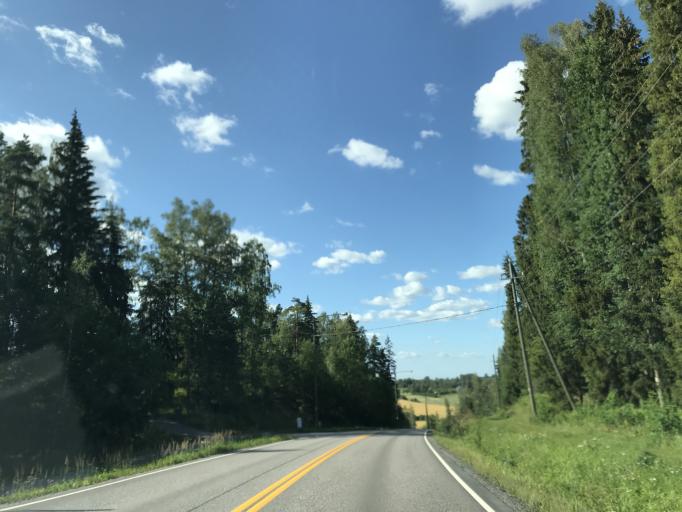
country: FI
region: Uusimaa
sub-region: Helsinki
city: Nurmijaervi
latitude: 60.4146
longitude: 24.8759
